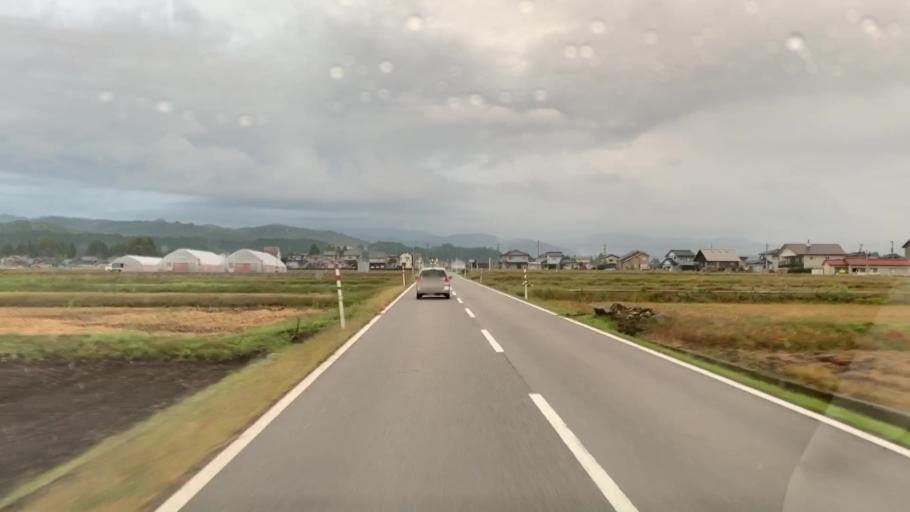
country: JP
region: Toyama
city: Kamiichi
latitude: 36.6344
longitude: 137.3285
